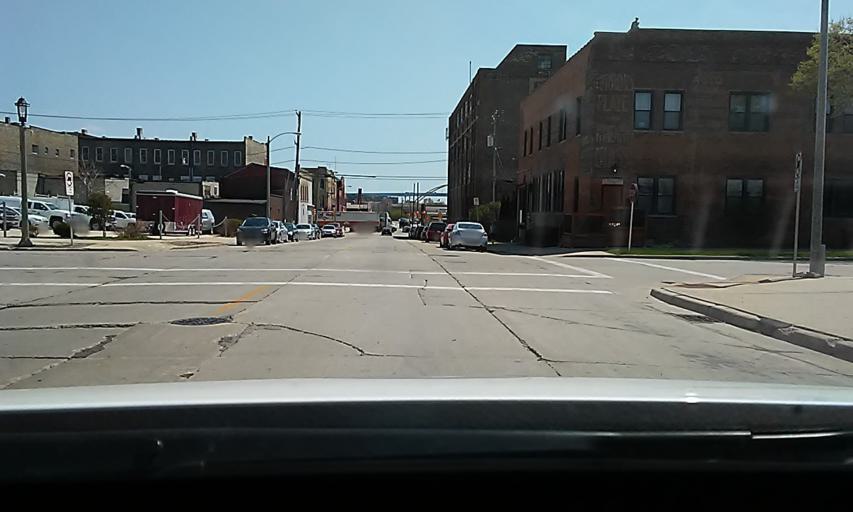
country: US
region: Wisconsin
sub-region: Milwaukee County
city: Milwaukee
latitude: 43.0263
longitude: -87.9143
